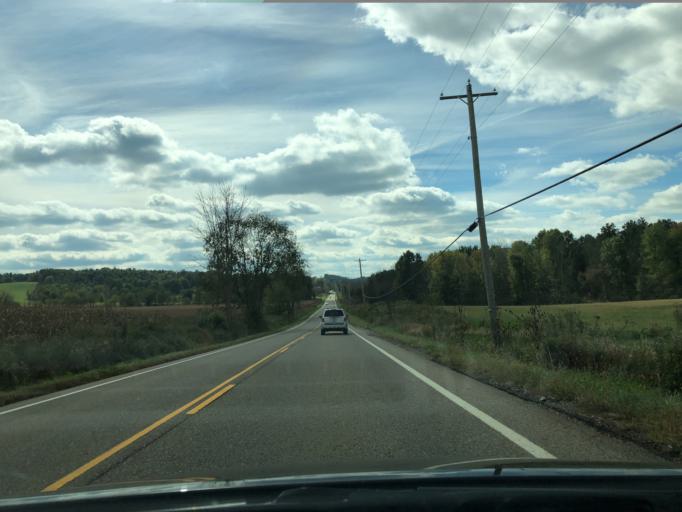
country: US
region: Ohio
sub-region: Stark County
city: Beach City
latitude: 40.6682
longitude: -81.6225
